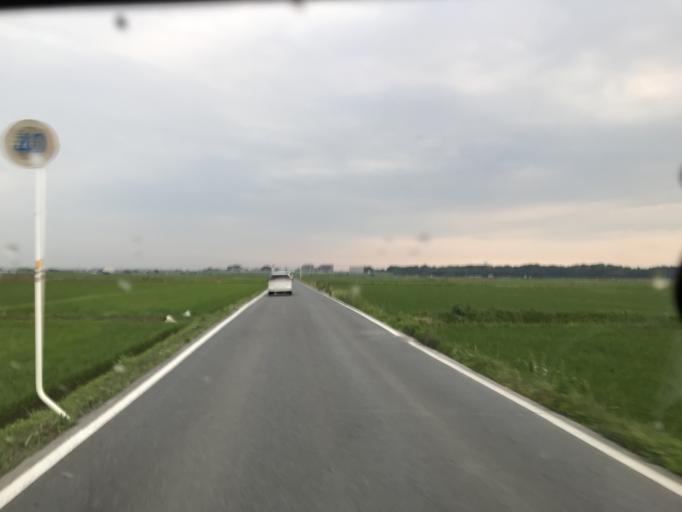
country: JP
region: Chiba
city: Abiko
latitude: 35.8912
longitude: 140.0287
